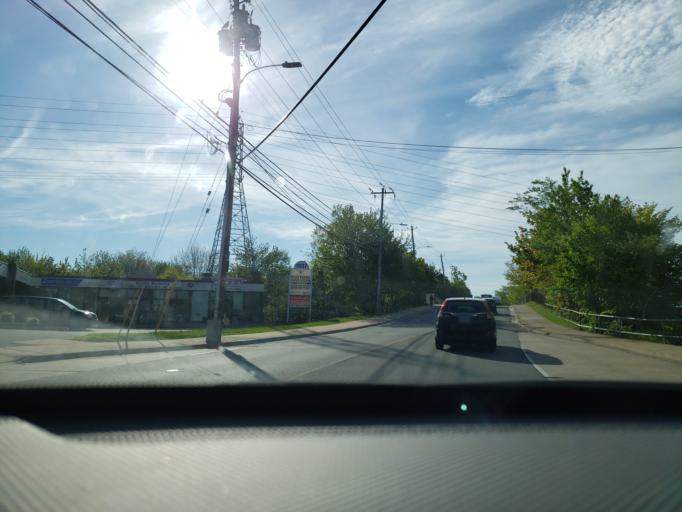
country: CA
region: Nova Scotia
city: Dartmouth
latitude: 44.6495
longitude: -63.6243
